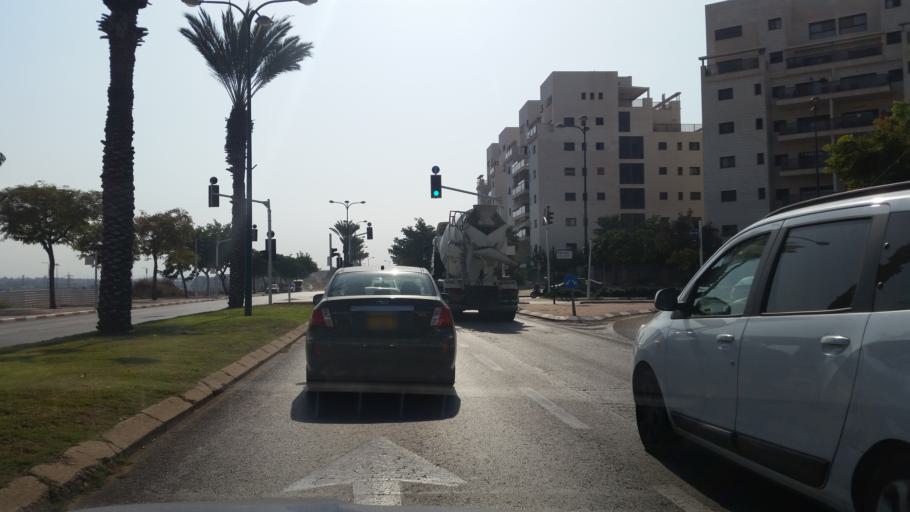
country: IL
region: Central District
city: Even Yehuda
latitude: 32.2908
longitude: 34.8537
